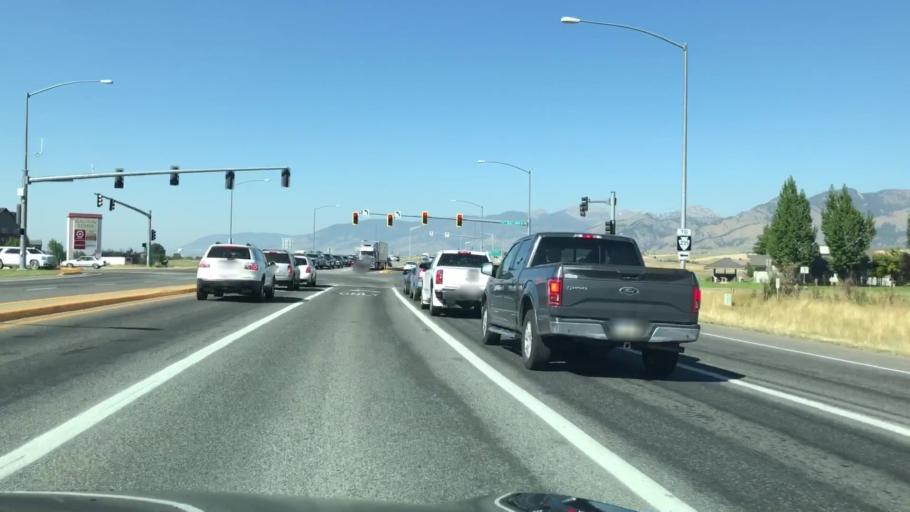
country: US
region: Montana
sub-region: Gallatin County
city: Bozeman
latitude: 45.7110
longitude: -111.0654
